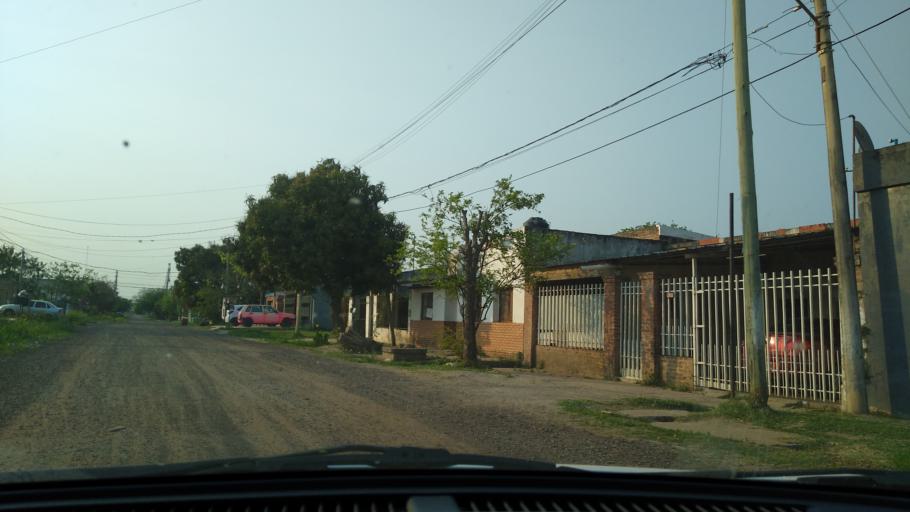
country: AR
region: Chaco
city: Barranqueras
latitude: -27.4851
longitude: -58.9297
